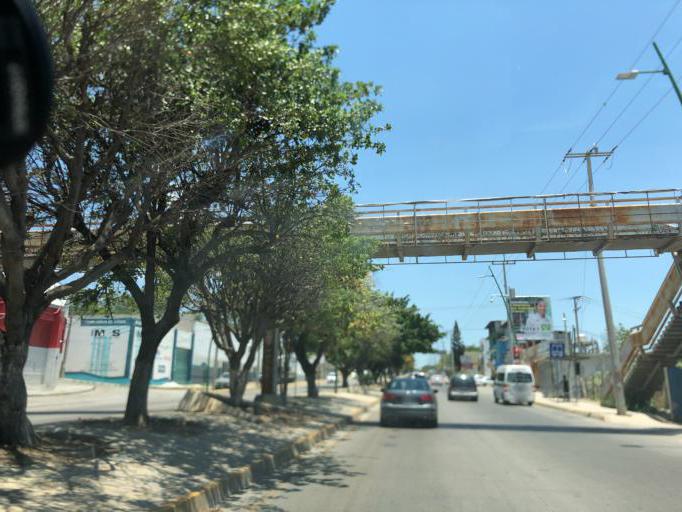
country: MX
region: Chiapas
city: Tuxtla Gutierrez
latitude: 16.7449
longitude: -93.1320
